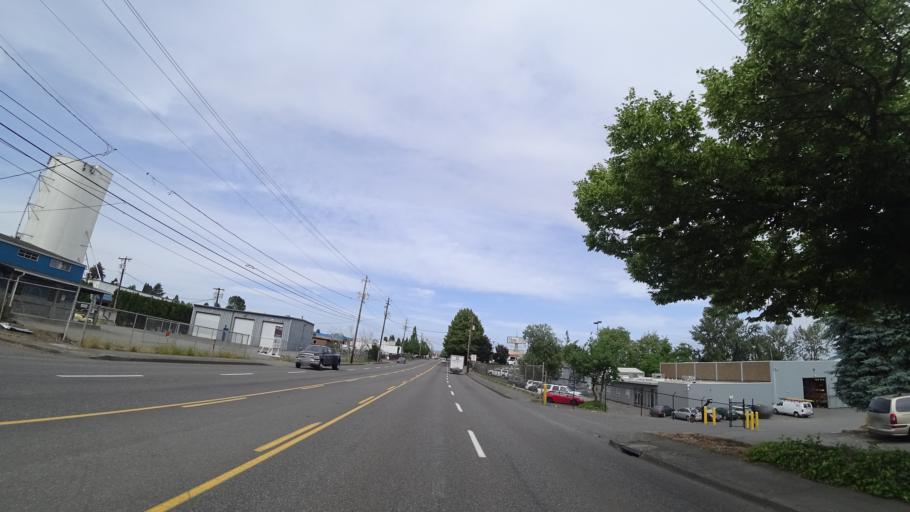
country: US
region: Oregon
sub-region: Multnomah County
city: Portland
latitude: 45.5754
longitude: -122.6388
